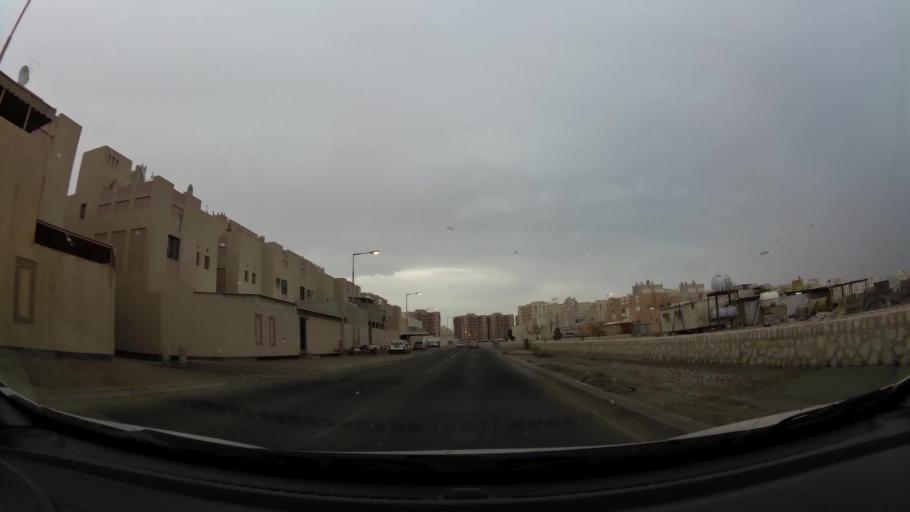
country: BH
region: Central Governorate
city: Madinat Hamad
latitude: 26.1252
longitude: 50.4883
